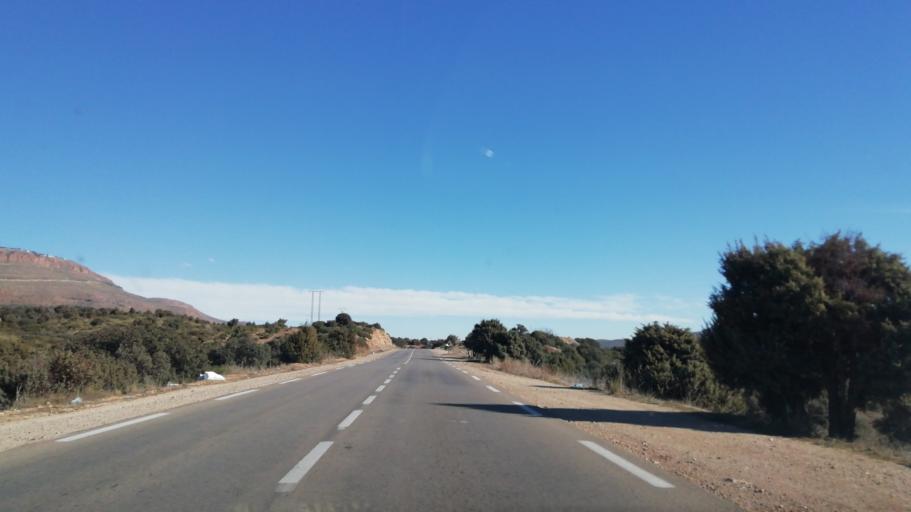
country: DZ
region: Tlemcen
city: Sebdou
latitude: 34.7201
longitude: -1.2003
